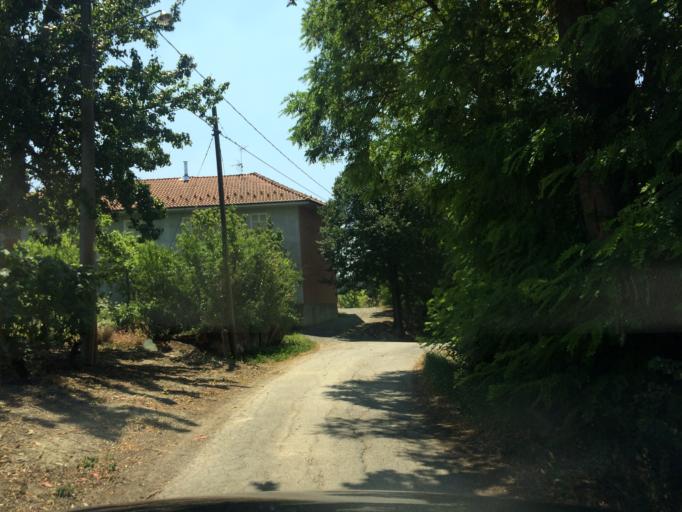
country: IT
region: Piedmont
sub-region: Provincia di Asti
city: Moasca
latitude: 44.7617
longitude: 8.2605
